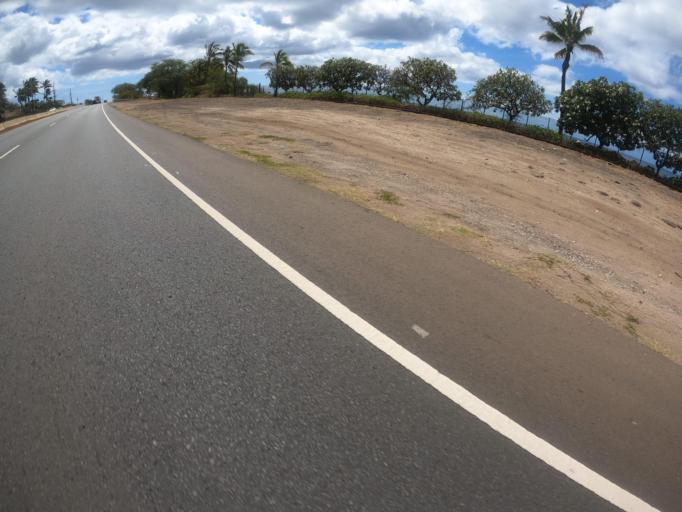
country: US
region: Hawaii
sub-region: Honolulu County
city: Makakilo
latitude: 21.3549
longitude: -158.1298
